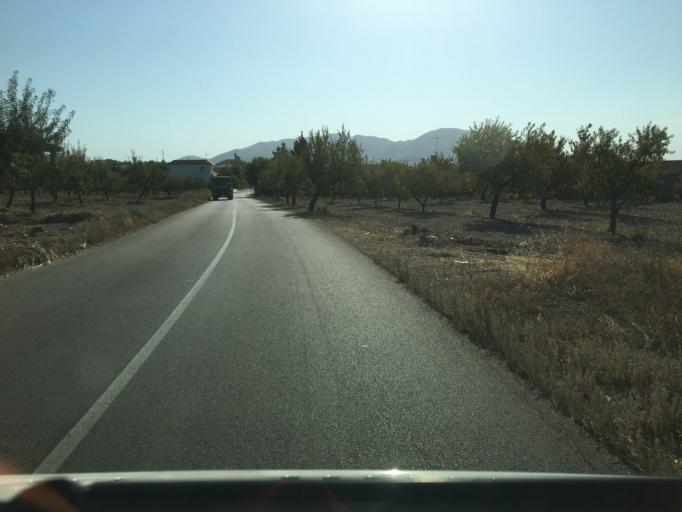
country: ES
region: Andalusia
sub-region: Provincia de Almeria
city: Huercal-Overa
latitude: 37.4700
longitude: -1.8963
